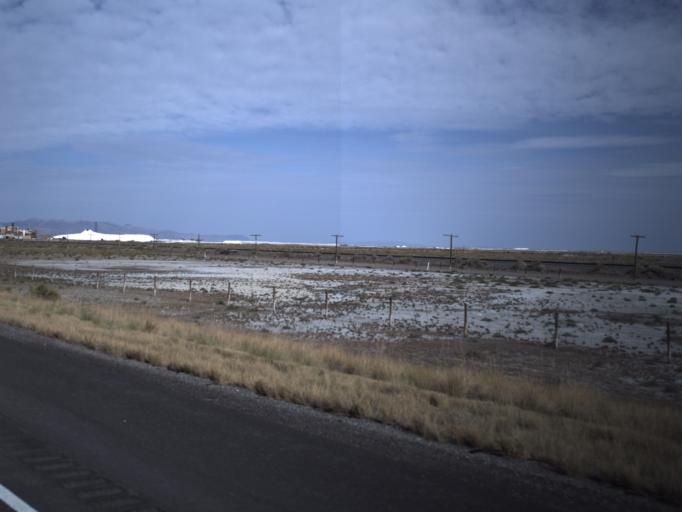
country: US
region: Utah
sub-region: Tooele County
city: Grantsville
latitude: 40.7019
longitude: -112.4925
